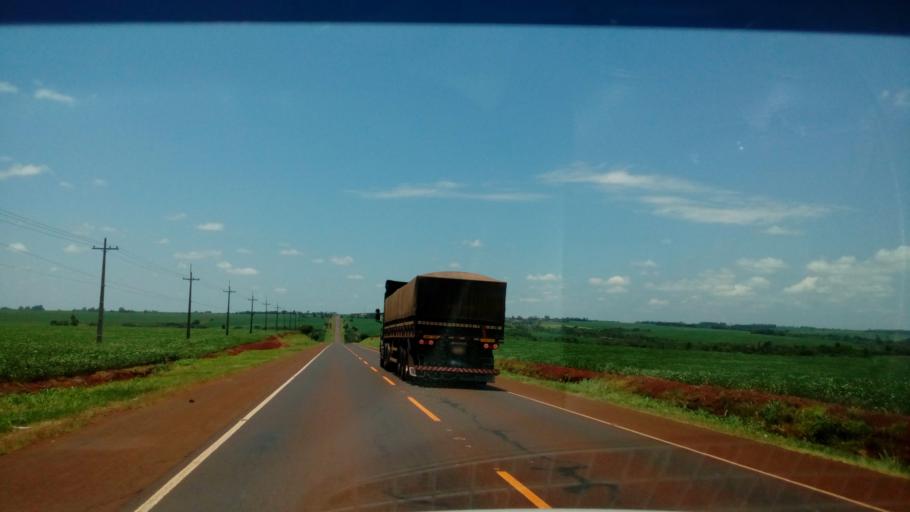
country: PY
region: Alto Parana
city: Naranjal
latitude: -25.8981
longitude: -55.1206
